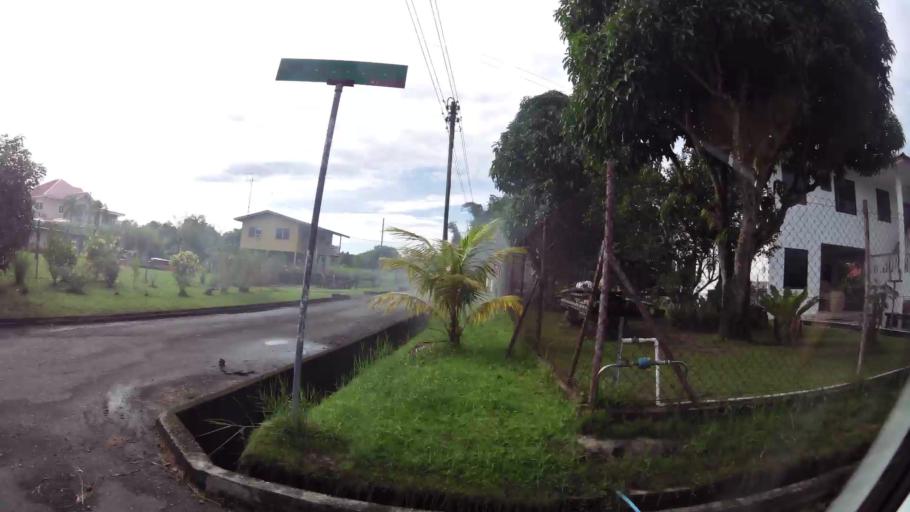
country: BN
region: Belait
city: Seria
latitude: 4.6149
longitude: 114.3620
